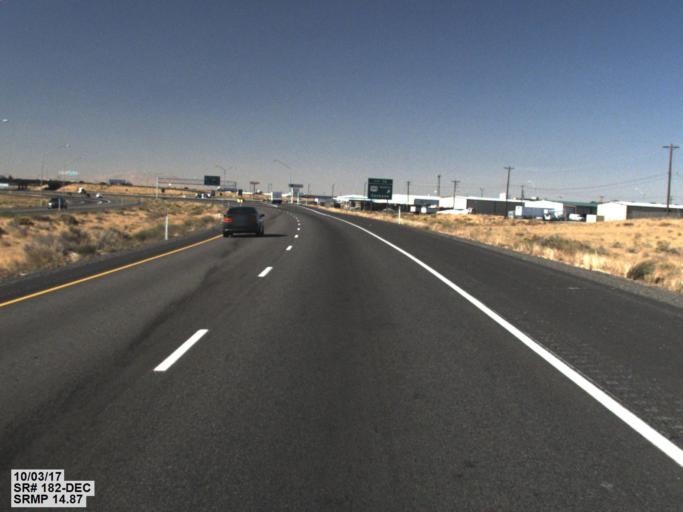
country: US
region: Washington
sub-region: Franklin County
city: Pasco
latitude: 46.2501
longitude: -119.0726
